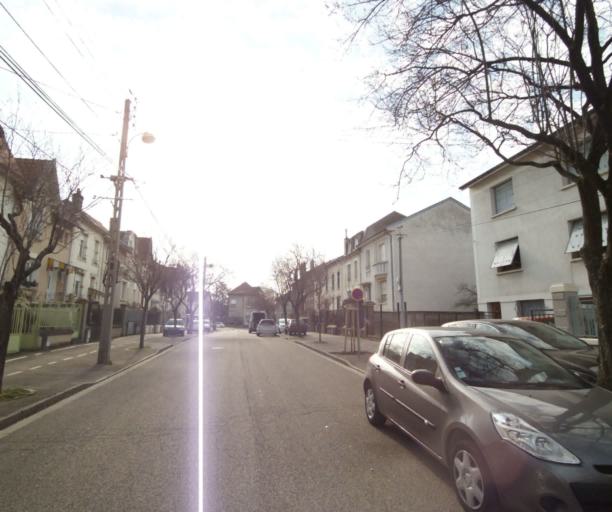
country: FR
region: Lorraine
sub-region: Departement de Meurthe-et-Moselle
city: Villers-les-Nancy
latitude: 48.6784
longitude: 6.1575
